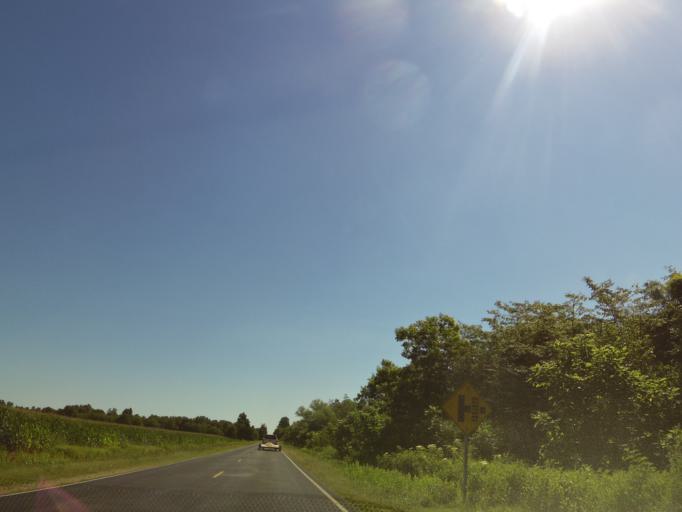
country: US
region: Missouri
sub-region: Dunklin County
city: Campbell
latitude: 36.4766
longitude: -90.1021
